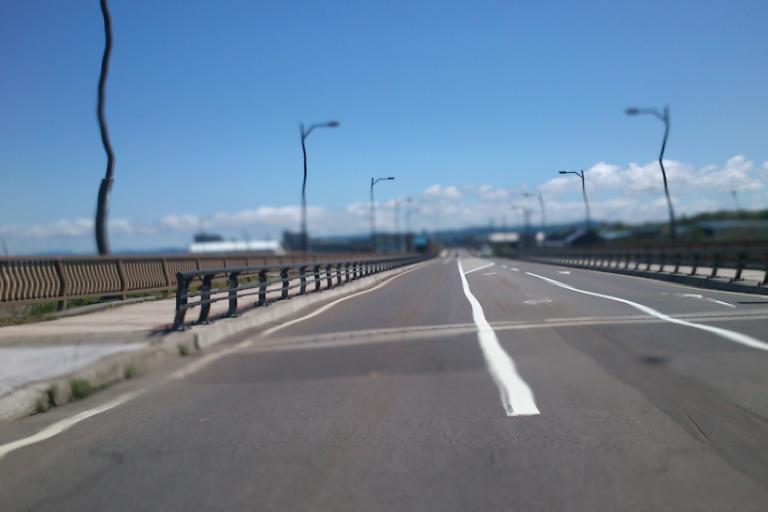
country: JP
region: Hokkaido
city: Rumoi
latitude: 43.8544
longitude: 141.5102
